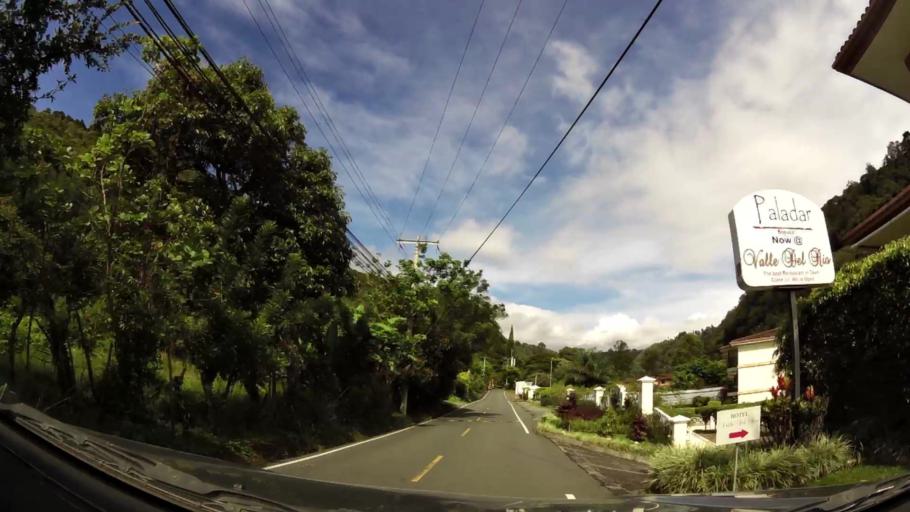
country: PA
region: Chiriqui
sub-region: Distrito Boquete
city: Boquete
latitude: 8.7769
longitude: -82.4377
